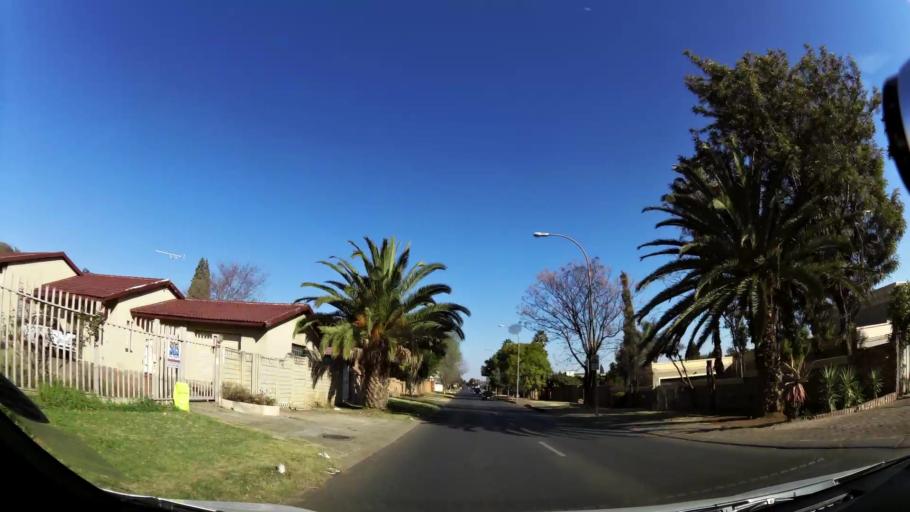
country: ZA
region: Gauteng
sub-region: City of Johannesburg Metropolitan Municipality
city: Johannesburg
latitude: -26.2935
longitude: 28.0539
